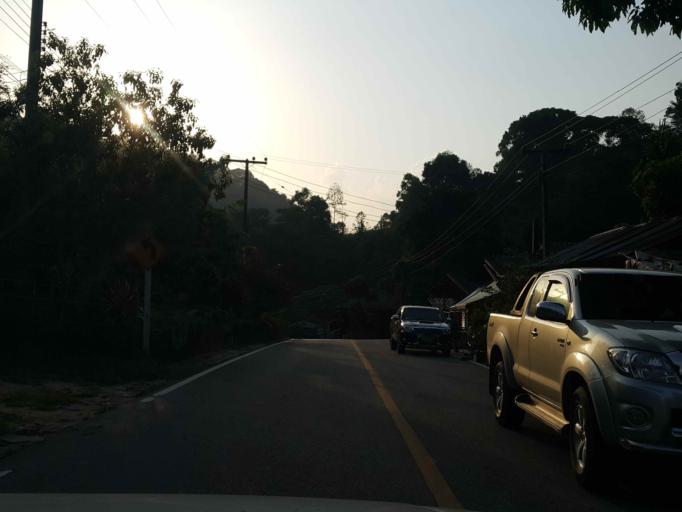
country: TH
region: Chiang Mai
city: Mae On
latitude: 18.9516
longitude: 99.3484
